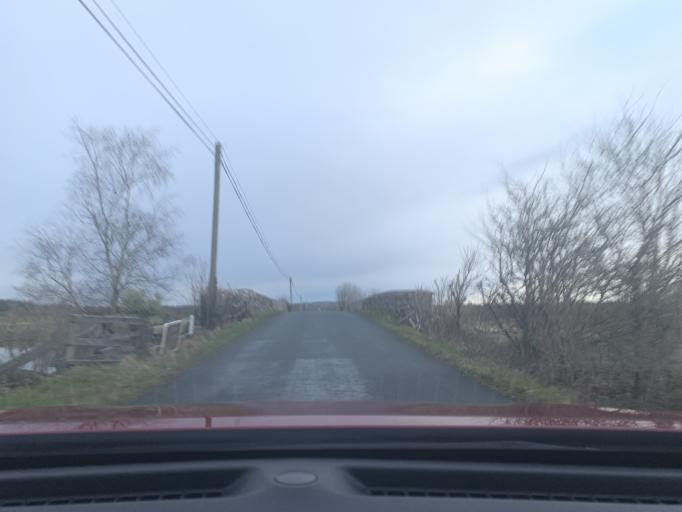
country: IE
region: Connaught
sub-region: Roscommon
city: Ballaghaderreen
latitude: 53.8849
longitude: -8.5676
